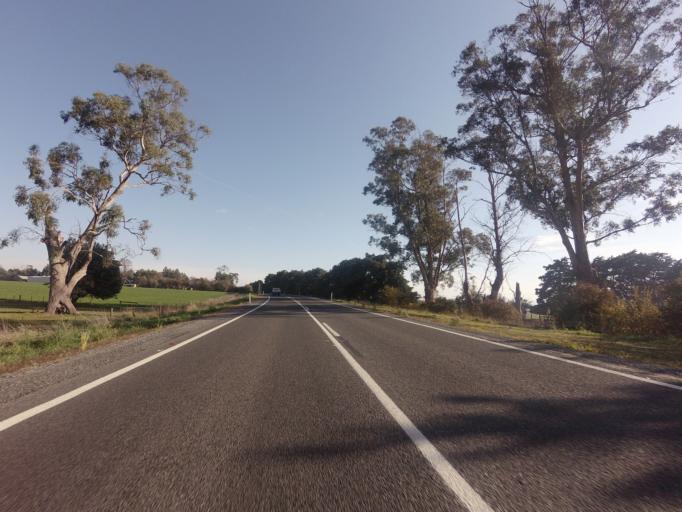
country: AU
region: Tasmania
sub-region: Northern Midlands
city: Longford
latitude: -41.5718
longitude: 147.0976
